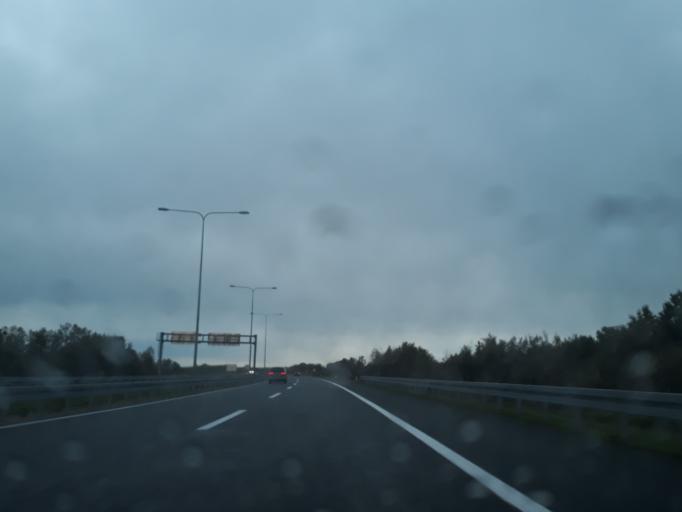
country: BA
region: Republika Srpska
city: Bosanska Gradiska
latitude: 45.0418
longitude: 17.2149
